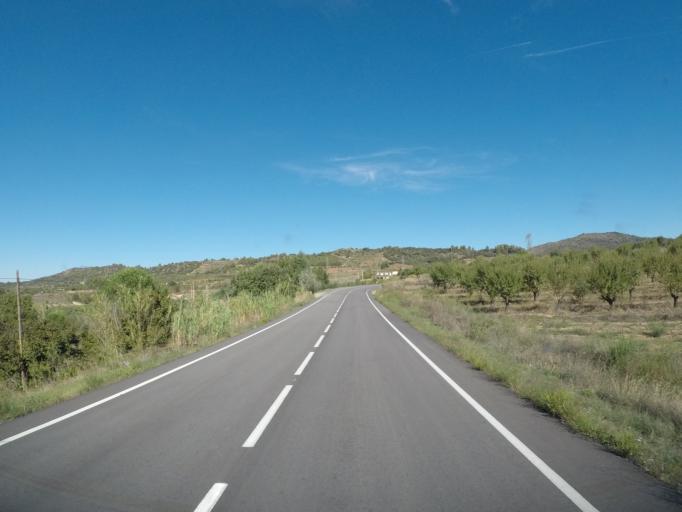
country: ES
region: Catalonia
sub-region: Provincia de Tarragona
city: Falset
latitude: 41.1560
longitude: 0.8152
